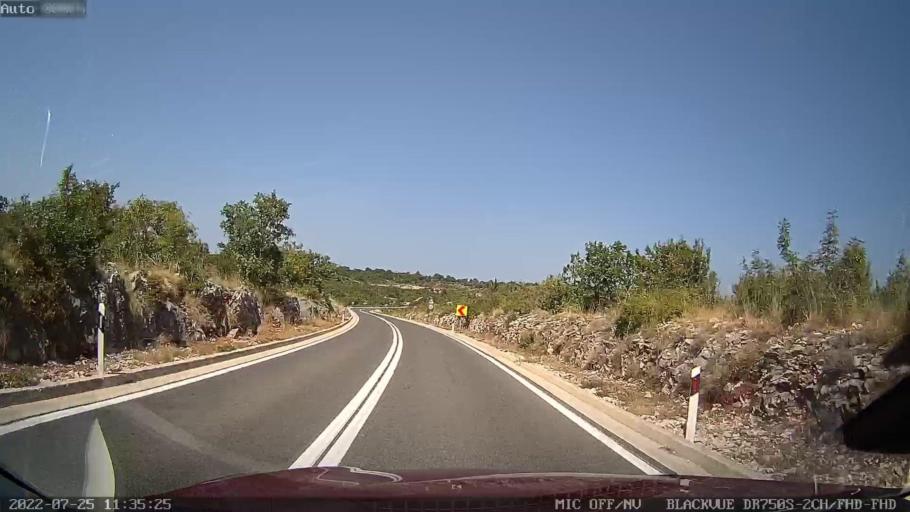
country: HR
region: Zadarska
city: Policnik
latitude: 44.2334
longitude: 15.4086
